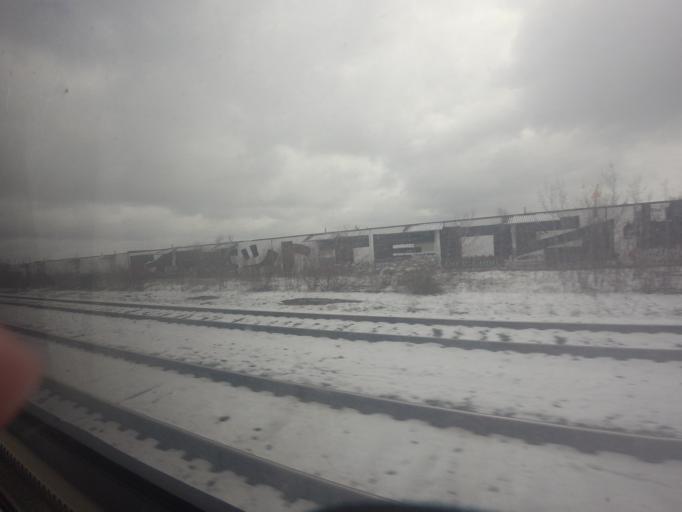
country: CA
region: Ontario
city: Scarborough
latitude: 43.7270
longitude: -79.2483
